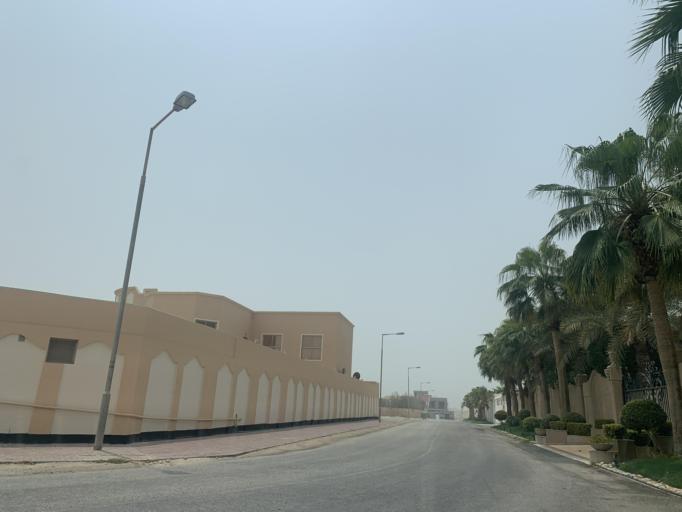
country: BH
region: Central Governorate
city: Madinat Hamad
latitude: 26.1654
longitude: 50.4792
